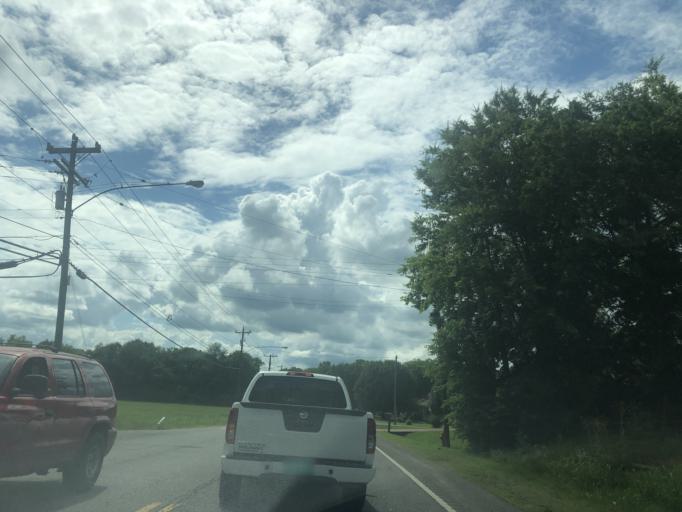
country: US
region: Tennessee
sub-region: Davidson County
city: Nashville
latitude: 36.2083
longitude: -86.8600
